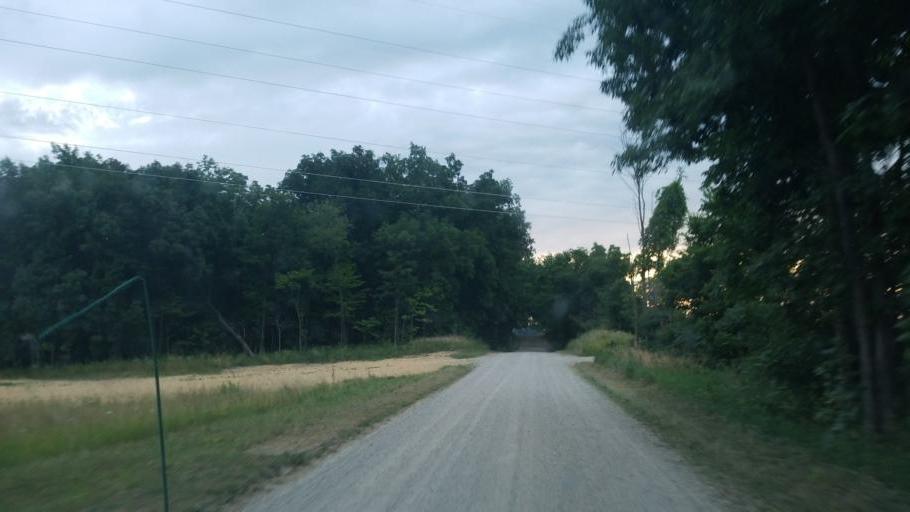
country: US
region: Ohio
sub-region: Defiance County
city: Hicksville
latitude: 41.3288
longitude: -84.8184
